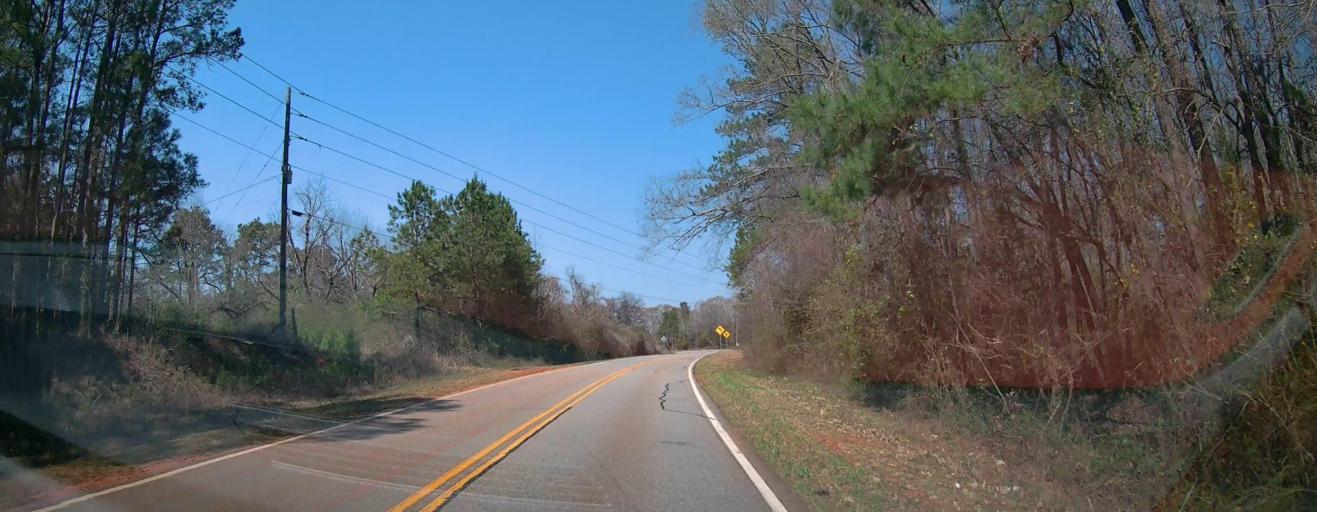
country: US
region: Georgia
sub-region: Peach County
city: Byron
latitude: 32.5827
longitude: -83.7599
